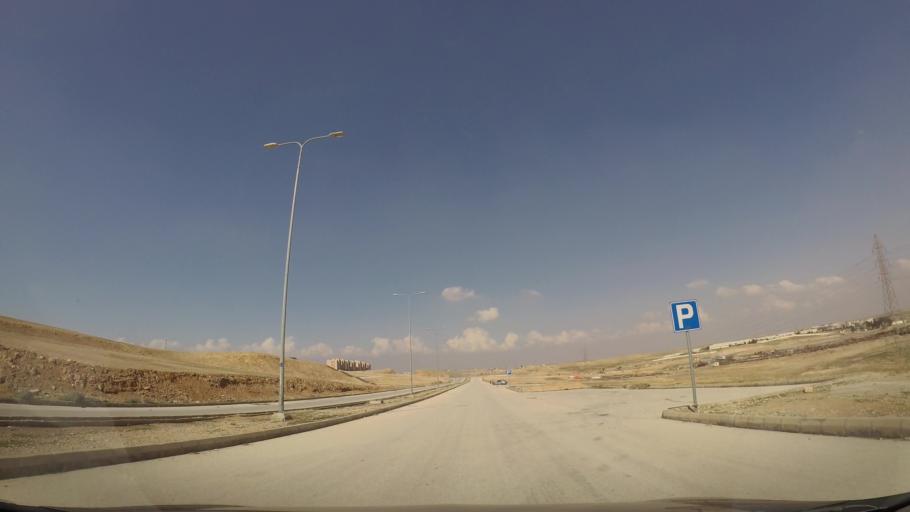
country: JO
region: Zarqa
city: Zarqa
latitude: 32.0513
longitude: 36.1234
